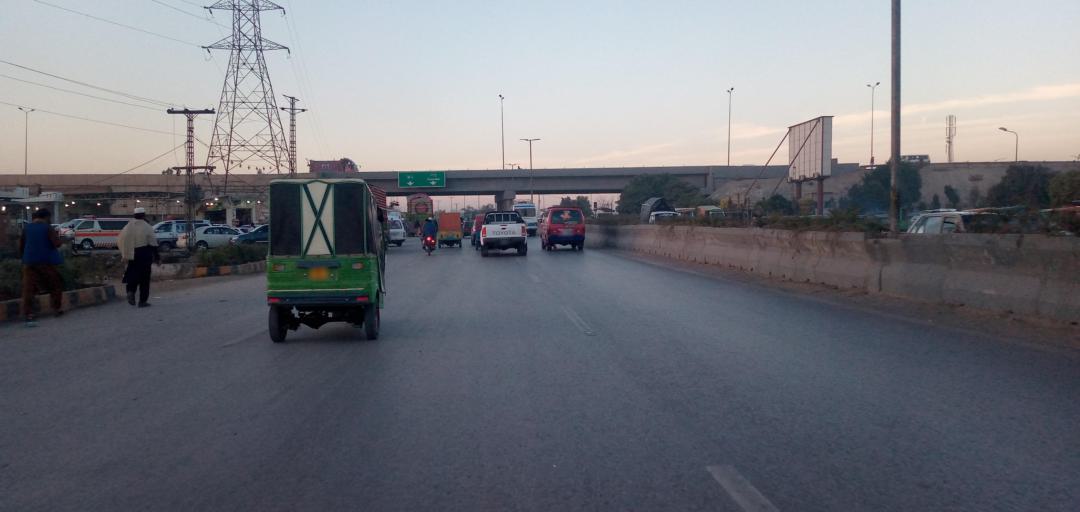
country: PK
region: Khyber Pakhtunkhwa
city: Peshawar
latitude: 34.0225
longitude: 71.6212
